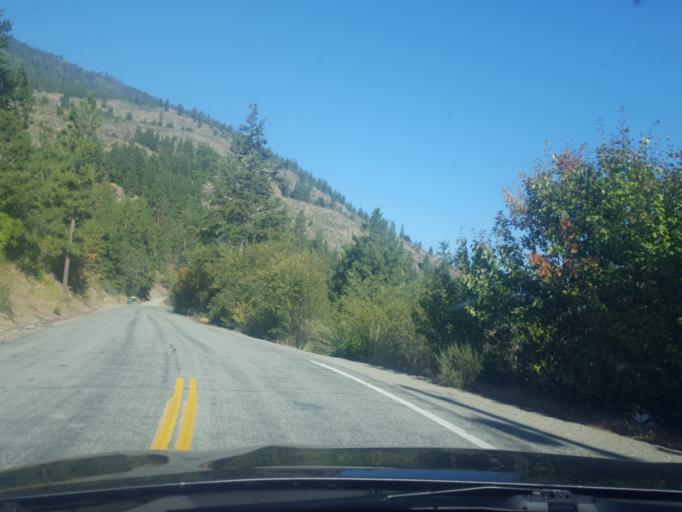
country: US
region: Washington
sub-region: Chelan County
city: Granite Falls
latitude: 47.9926
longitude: -120.2639
